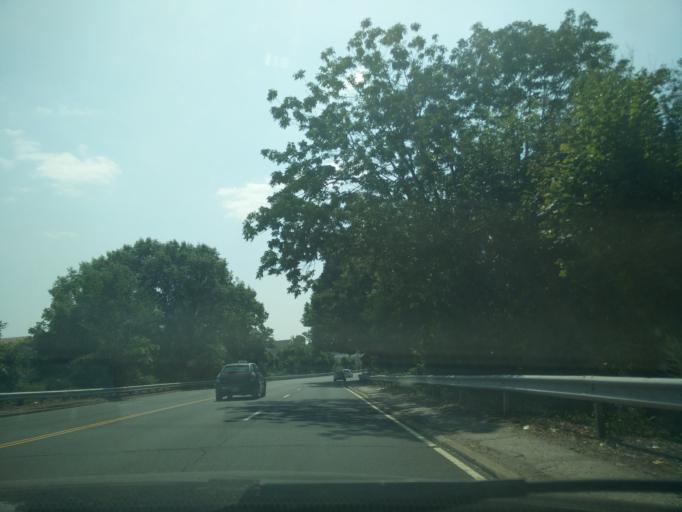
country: US
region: Connecticut
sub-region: Fairfield County
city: Fairfield
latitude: 41.1532
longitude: -73.2441
